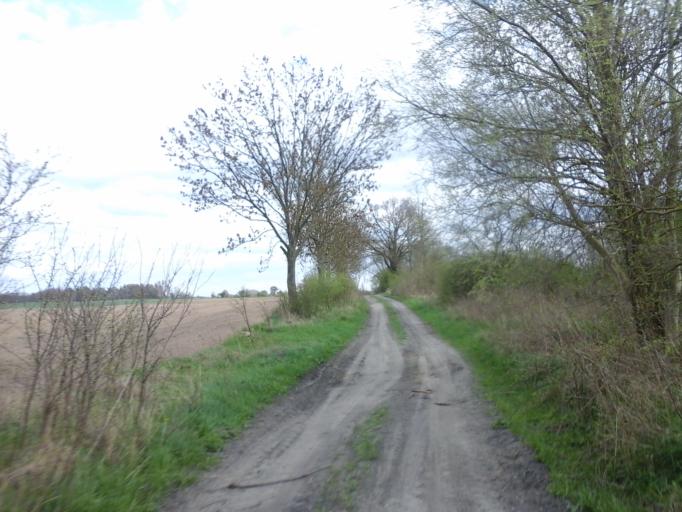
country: PL
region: West Pomeranian Voivodeship
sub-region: Powiat choszczenski
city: Krzecin
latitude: 53.1047
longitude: 15.5147
